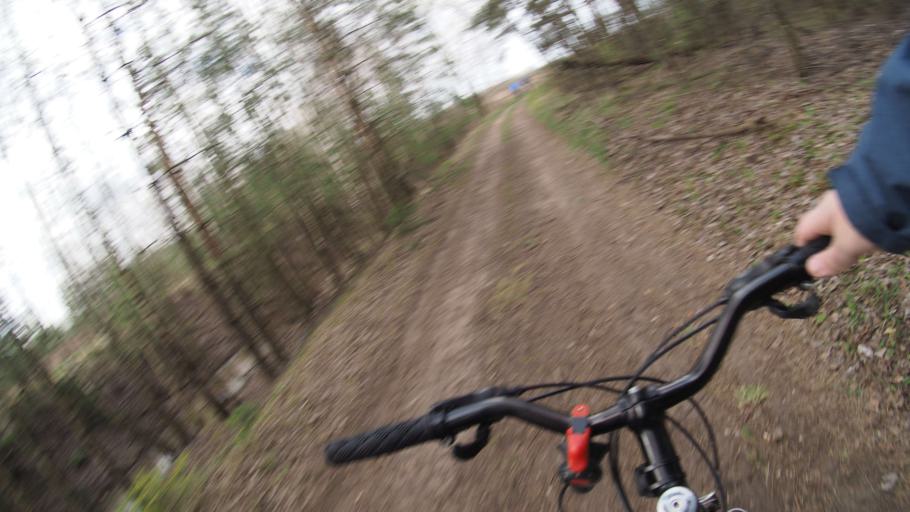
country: RU
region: Moskovskaya
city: Ramenskoye
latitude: 55.5973
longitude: 38.2870
